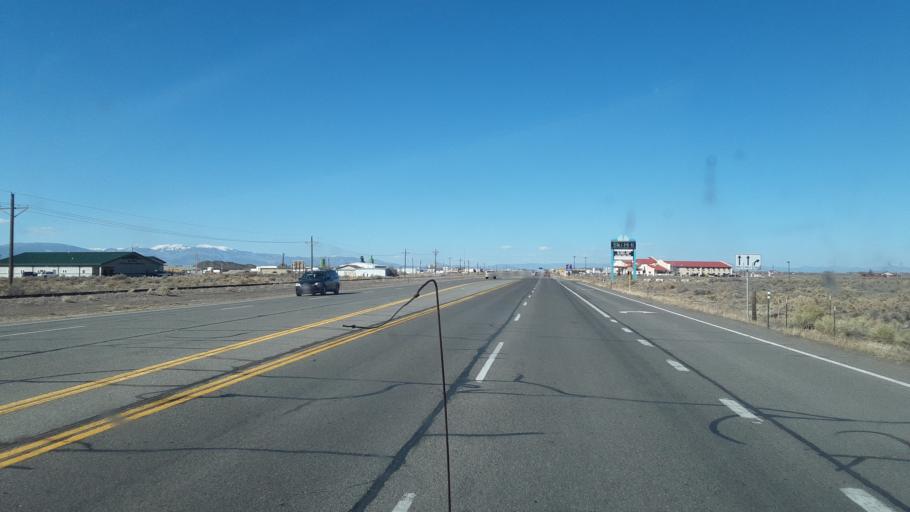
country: US
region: Colorado
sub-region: Alamosa County
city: Alamosa
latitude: 37.4811
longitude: -105.9084
